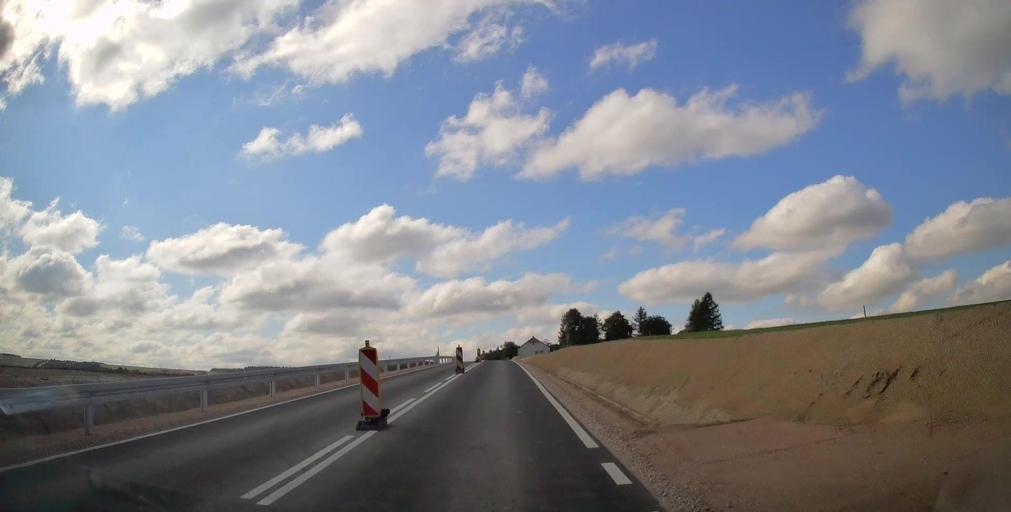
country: PL
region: Swietokrzyskie
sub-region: Powiat jedrzejowski
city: Wodzislaw
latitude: 50.4800
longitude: 20.1789
